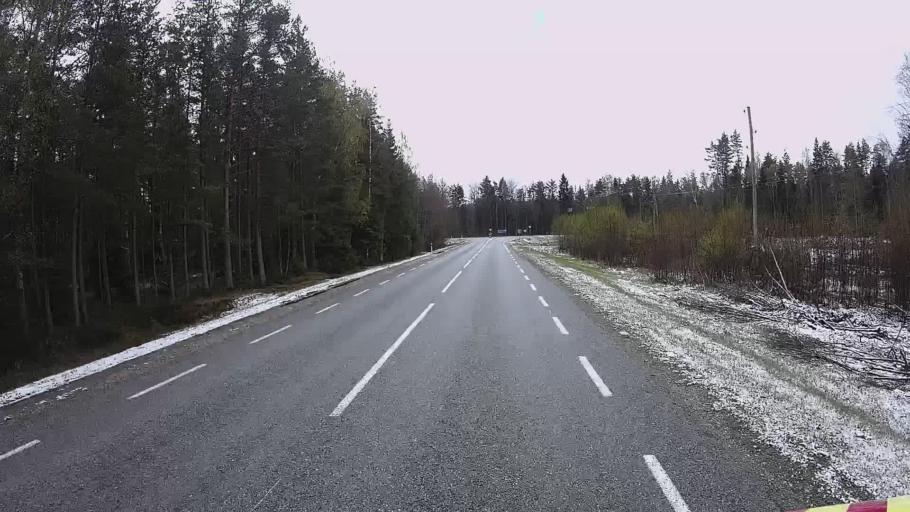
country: EE
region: Hiiumaa
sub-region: Kaerdla linn
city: Kardla
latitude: 59.0125
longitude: 22.6716
